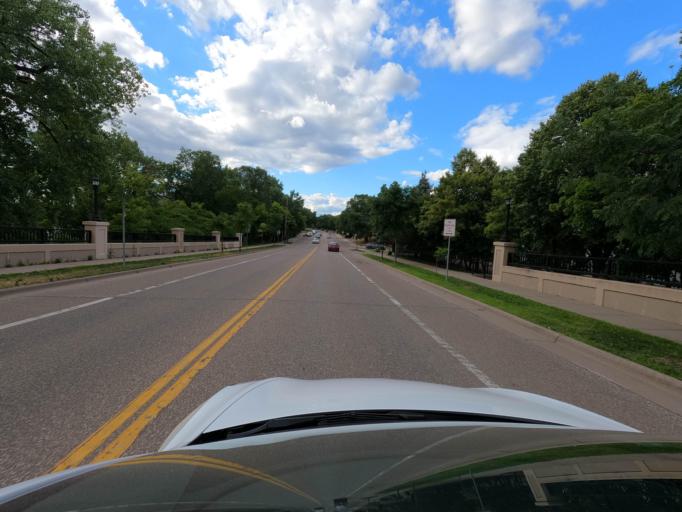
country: US
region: Minnesota
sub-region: Hennepin County
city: Minneapolis
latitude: 44.9895
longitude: -93.2609
